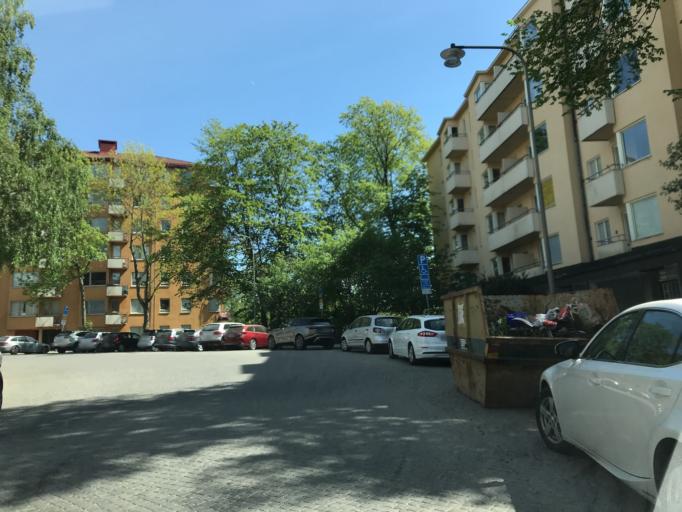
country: SE
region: Stockholm
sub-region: Stockholms Kommun
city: OEstermalm
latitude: 59.3455
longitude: 18.0995
